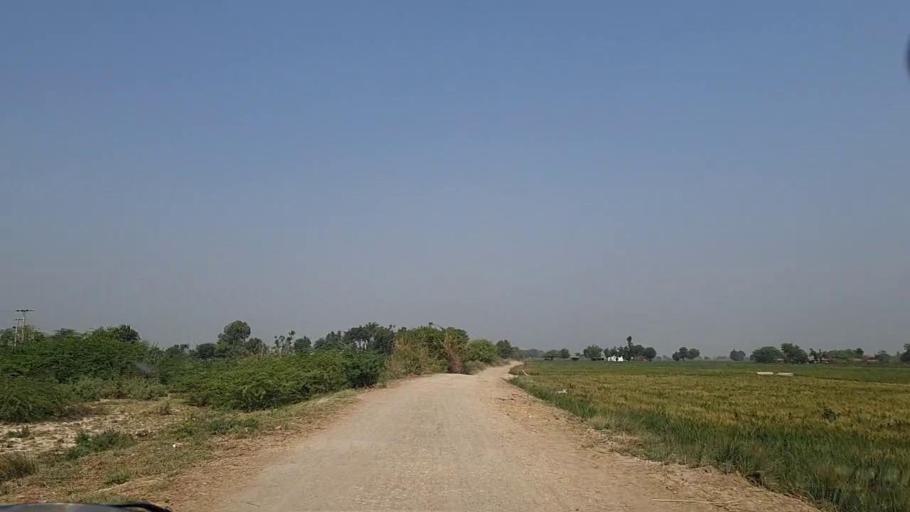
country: PK
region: Sindh
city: Mirpur Khas
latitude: 25.4985
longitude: 69.1908
